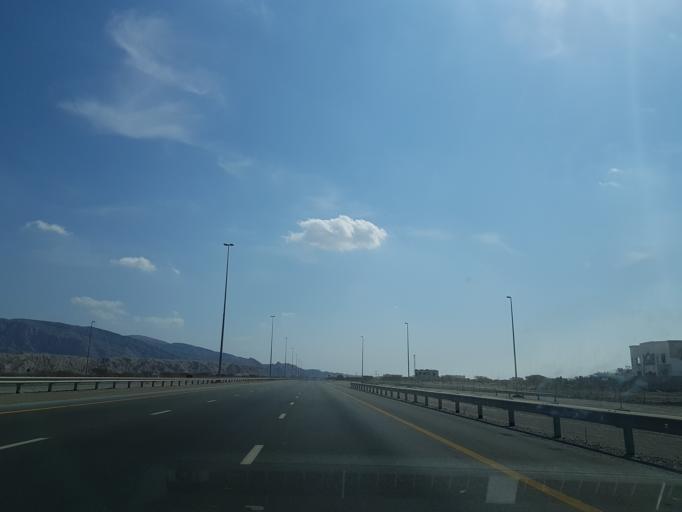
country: AE
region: Ra's al Khaymah
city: Ras al-Khaimah
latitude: 25.7964
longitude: 56.0307
